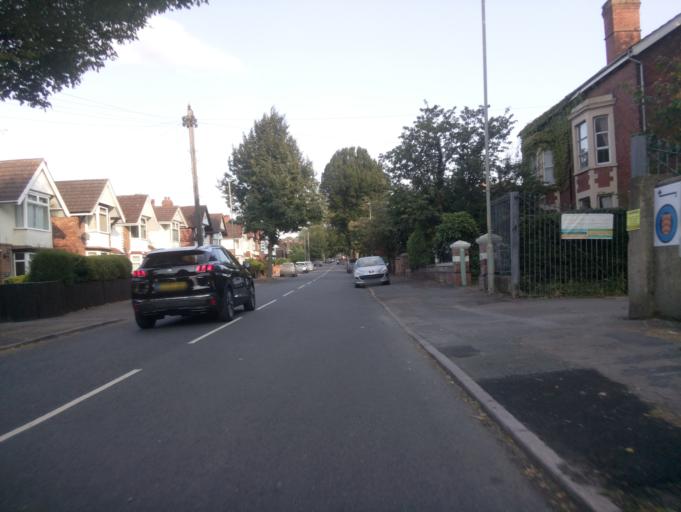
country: GB
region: England
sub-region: Gloucestershire
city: Gloucester
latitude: 51.8453
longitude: -2.2486
